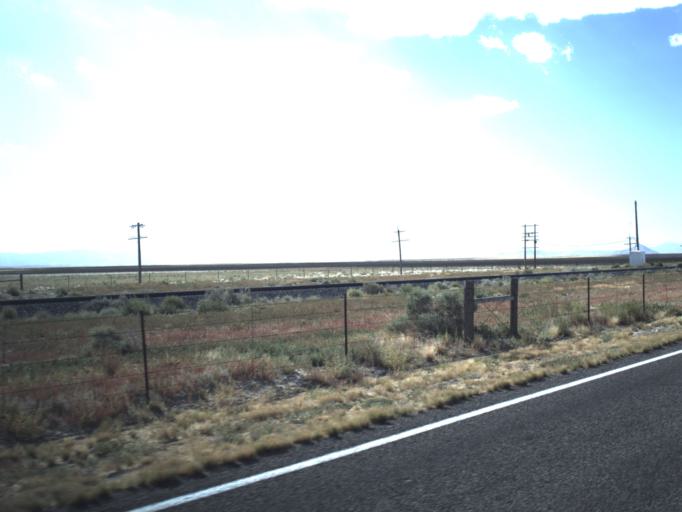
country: US
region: Utah
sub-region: Millard County
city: Delta
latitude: 39.0160
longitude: -112.7812
